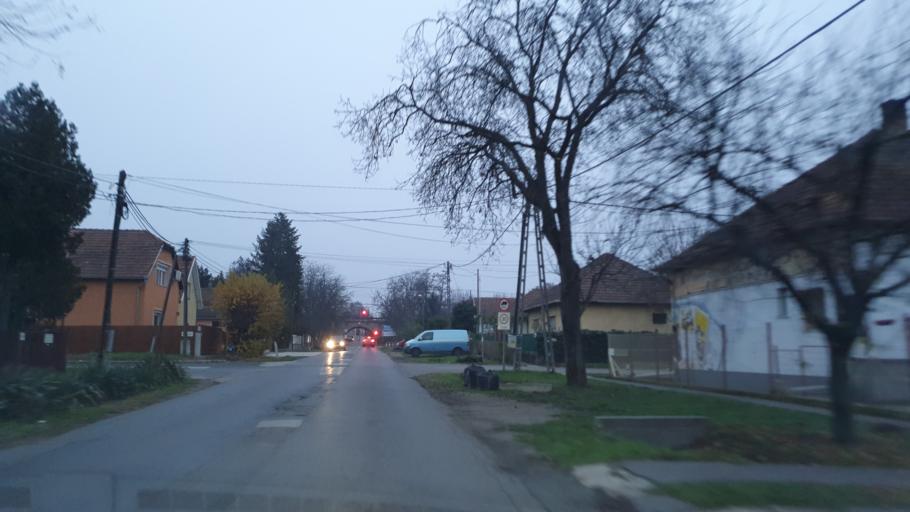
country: HU
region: Pest
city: Csomor
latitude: 47.5273
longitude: 19.2274
